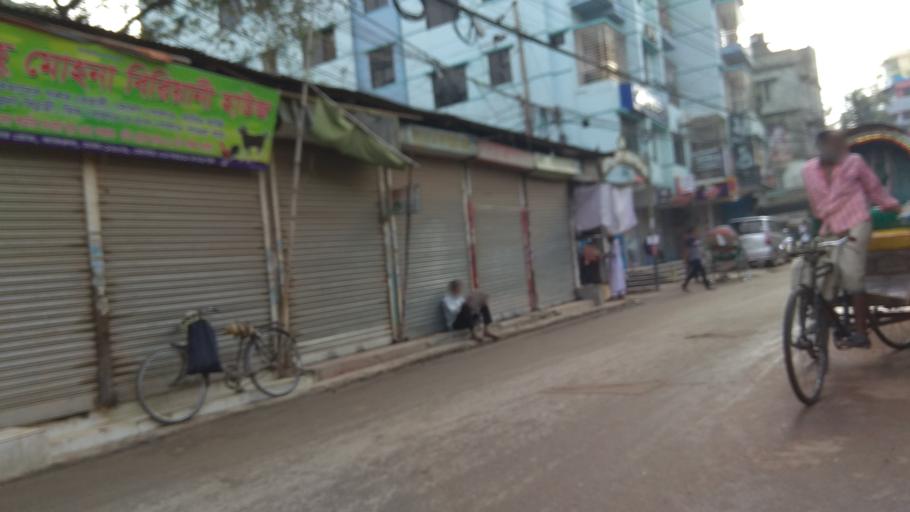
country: BD
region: Dhaka
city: Azimpur
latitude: 23.7943
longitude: 90.3822
